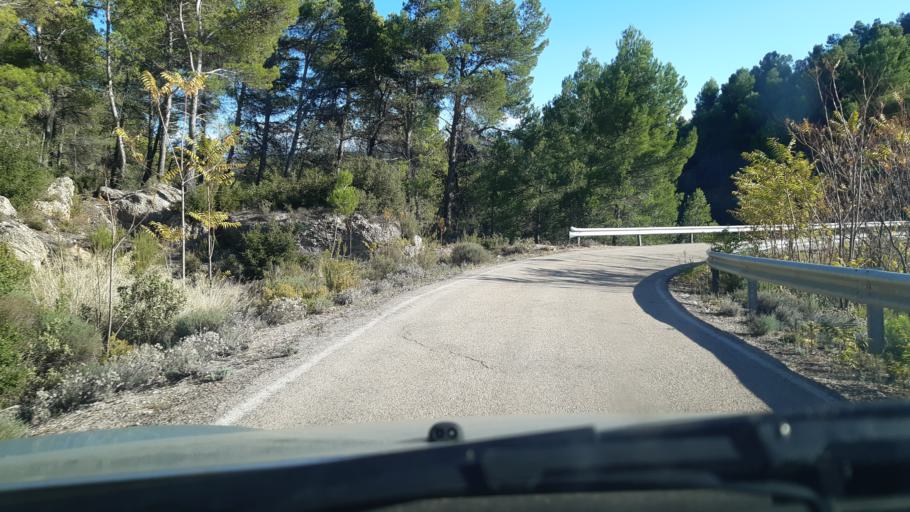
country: ES
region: Aragon
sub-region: Provincia de Teruel
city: Fornoles
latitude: 40.9093
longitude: -0.0146
